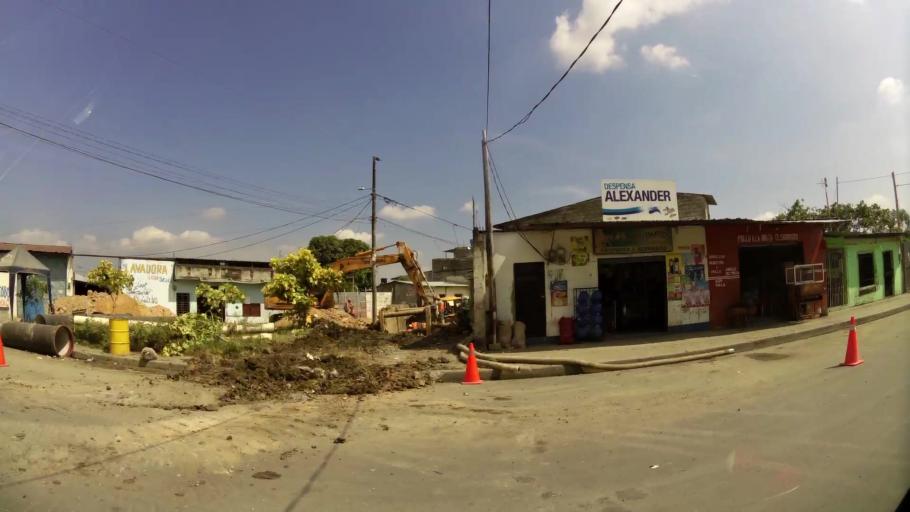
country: EC
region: Guayas
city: Eloy Alfaro
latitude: -2.1504
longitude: -79.8323
